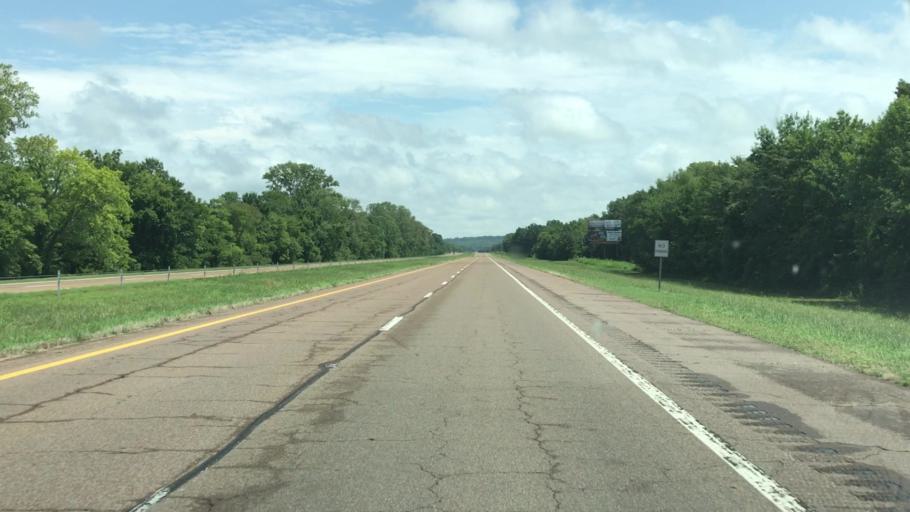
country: US
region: Missouri
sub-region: Pemiscot County
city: Caruthersville
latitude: 36.0831
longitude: -89.5405
